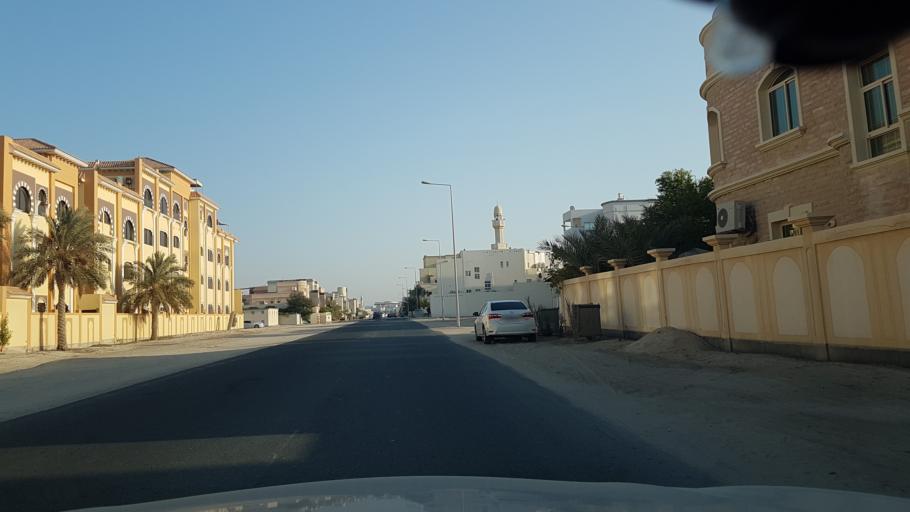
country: BH
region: Muharraq
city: Al Muharraq
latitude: 26.2783
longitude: 50.6030
